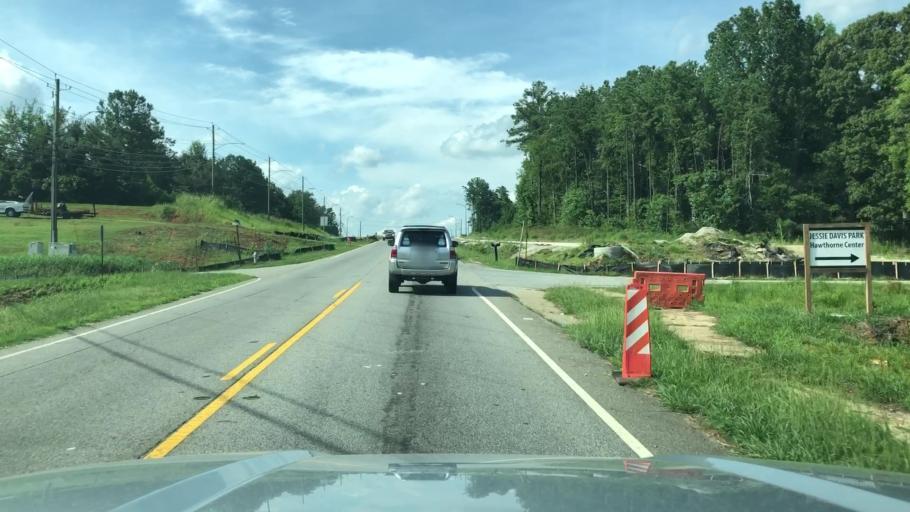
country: US
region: Georgia
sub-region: Douglas County
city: Douglasville
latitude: 33.7647
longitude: -84.7486
